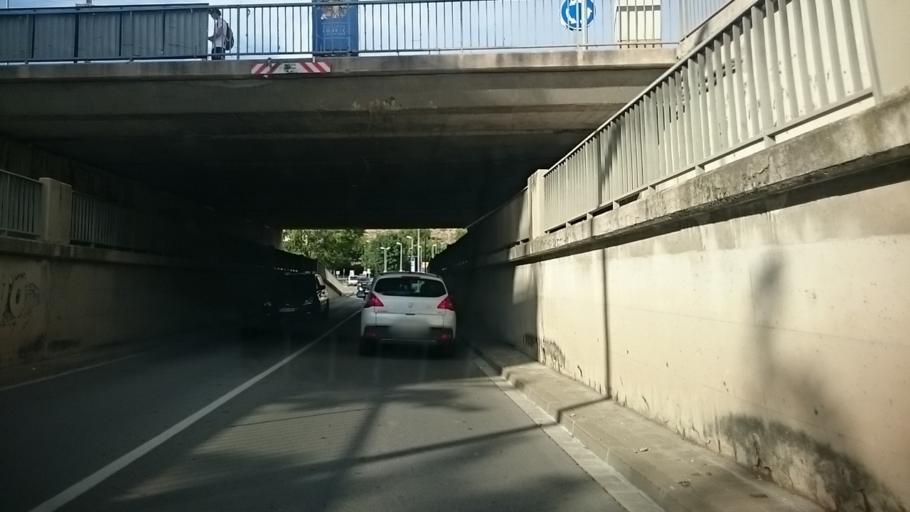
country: ES
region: Catalonia
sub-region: Provincia de Barcelona
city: Igualada
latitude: 41.5891
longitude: 1.6154
